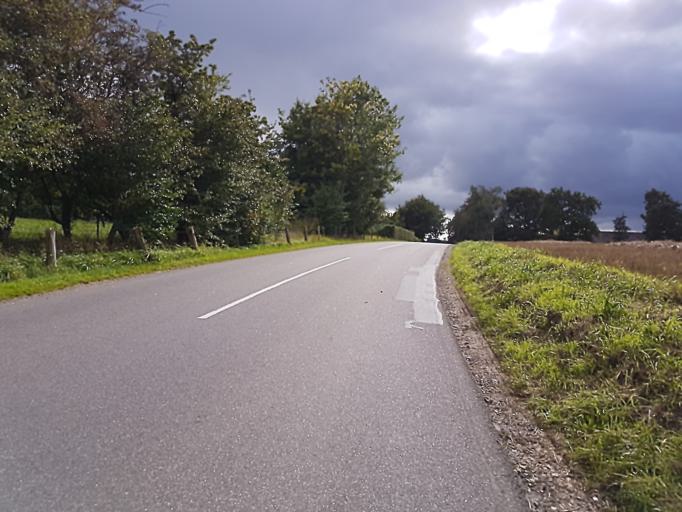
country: DK
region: Zealand
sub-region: Roskilde Kommune
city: Gundsomagle
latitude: 55.7219
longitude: 12.1376
